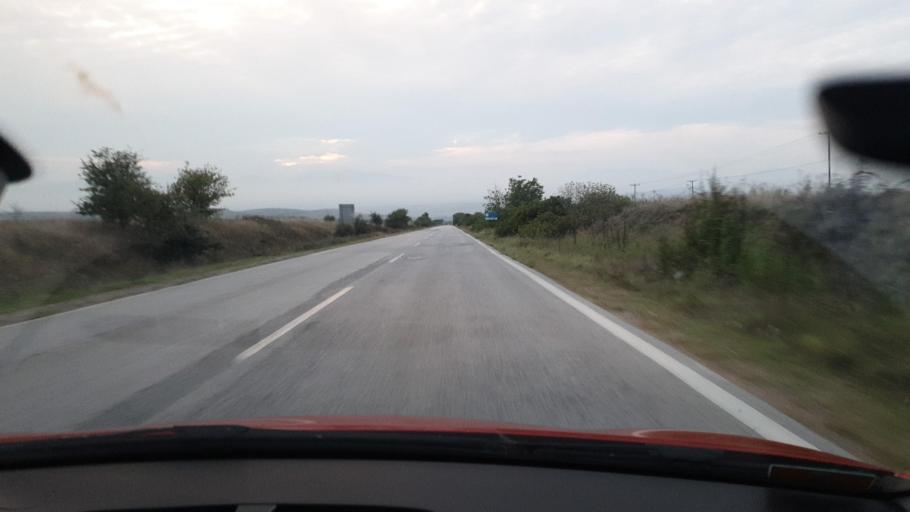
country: GR
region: Central Macedonia
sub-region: Nomos Kilkis
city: Polykastro
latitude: 41.0072
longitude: 22.6958
